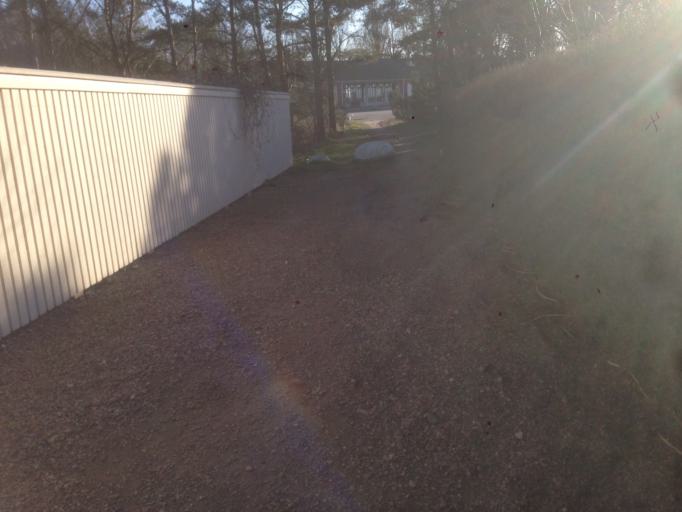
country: SE
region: Skane
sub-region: Vellinge Kommun
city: Hollviken
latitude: 55.4069
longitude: 13.0009
